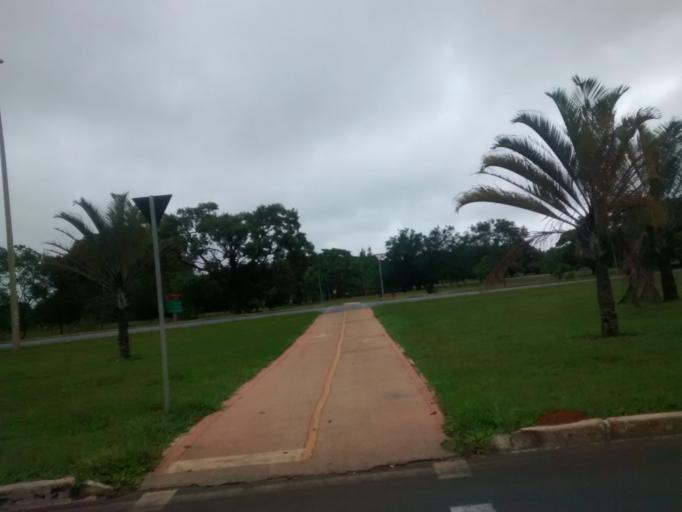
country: BR
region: Federal District
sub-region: Brasilia
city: Brasilia
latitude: -15.8041
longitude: -47.8523
